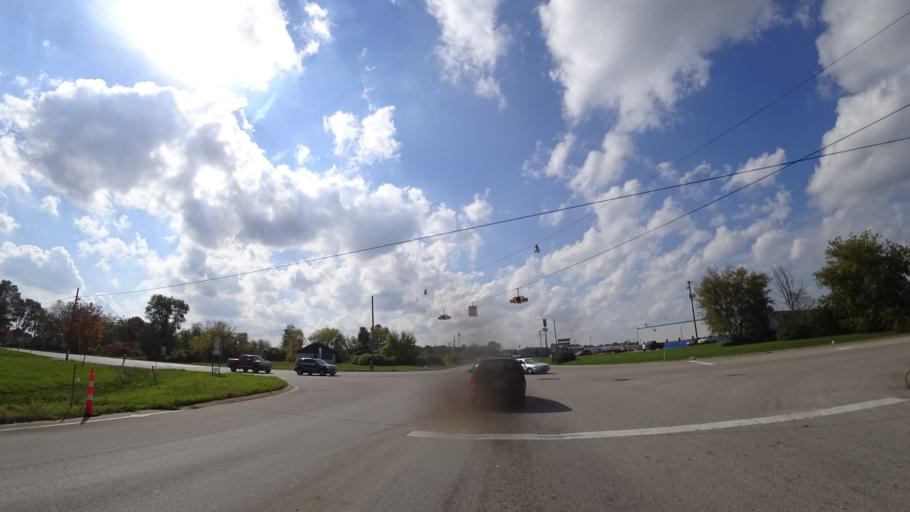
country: US
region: Michigan
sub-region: Branch County
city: Union City
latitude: 42.1066
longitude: -84.9863
